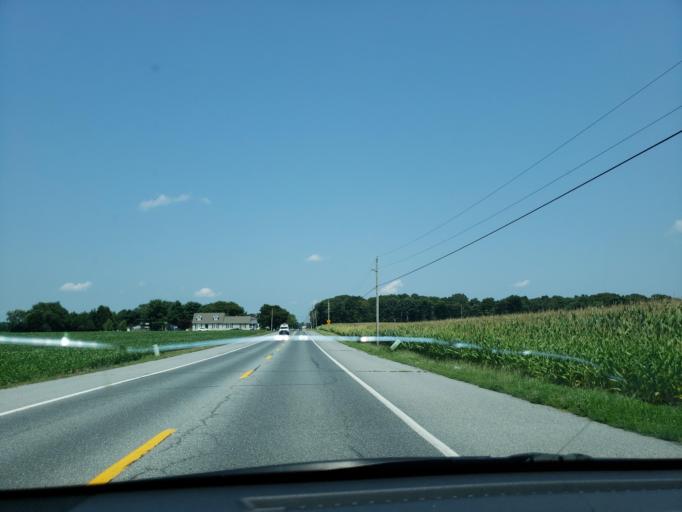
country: US
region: Delaware
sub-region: Sussex County
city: Milton
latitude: 38.7961
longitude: -75.3143
